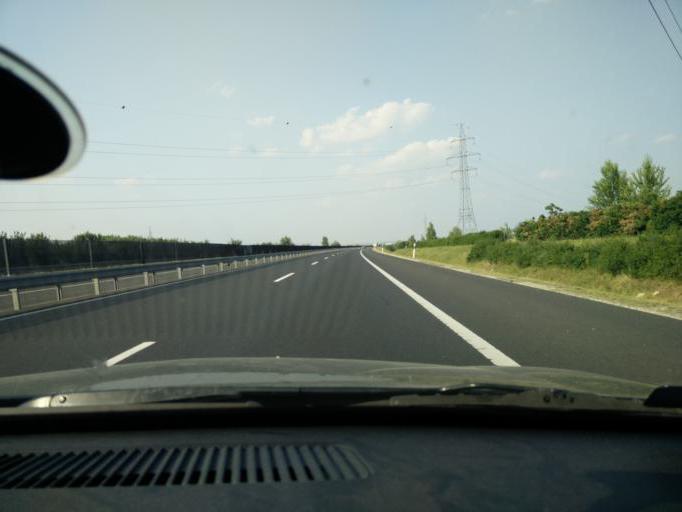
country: HU
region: Pest
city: Szazhalombatta
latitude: 47.3214
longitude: 18.8742
